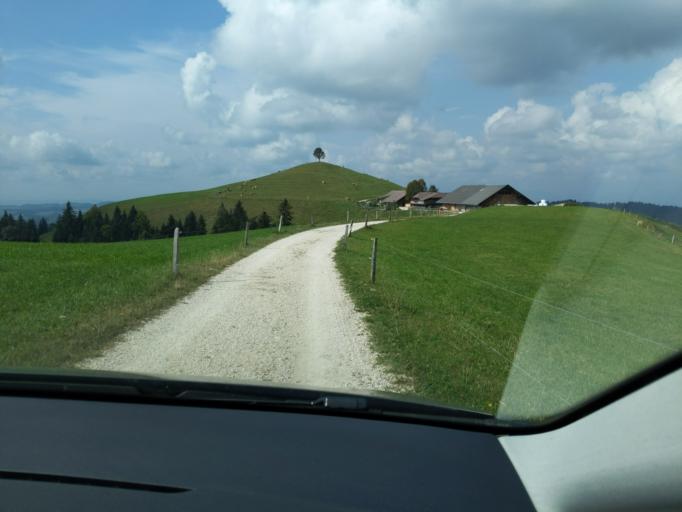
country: CH
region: Bern
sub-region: Oberaargau
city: Wyssachen
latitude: 47.0286
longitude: 7.8290
